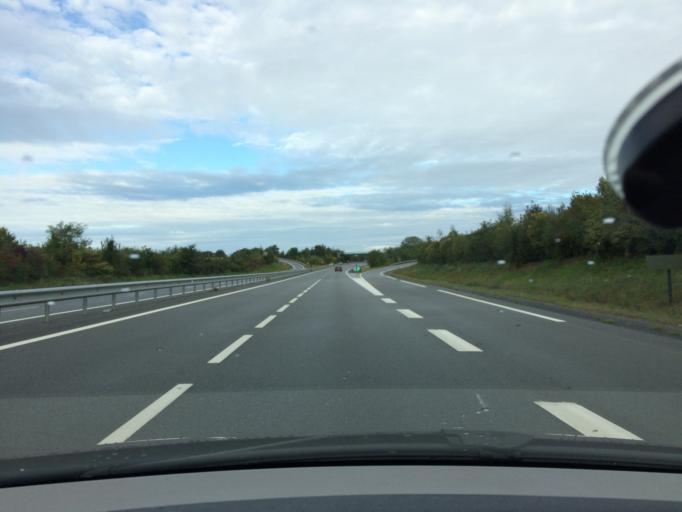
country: FR
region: Brittany
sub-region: Departement d'Ille-et-Vilaine
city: Corps-Nuds
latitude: 47.9775
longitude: -1.5558
